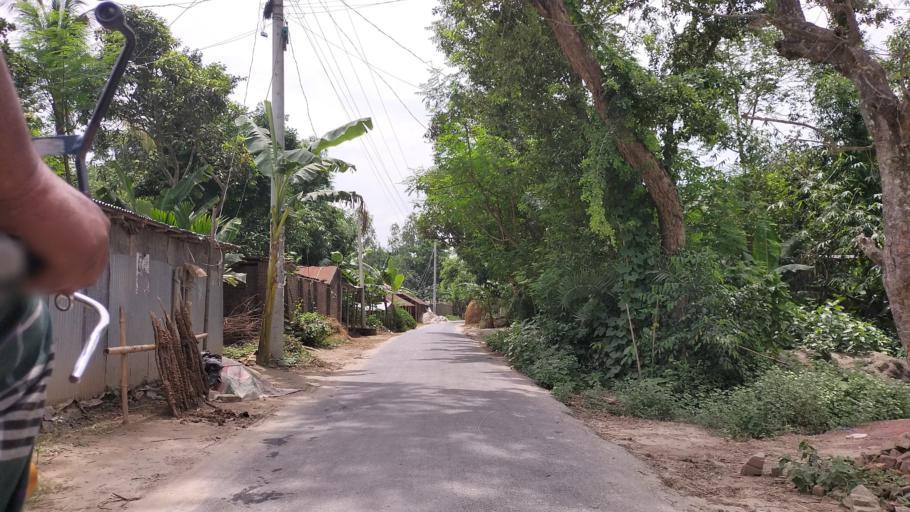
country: BD
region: Rajshahi
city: Rajshahi
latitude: 24.5153
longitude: 88.6285
